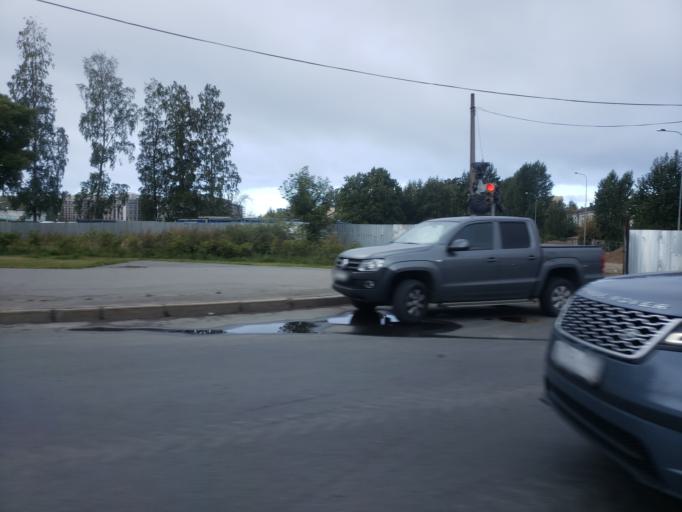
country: RU
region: St.-Petersburg
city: Vasyl'evsky Ostrov
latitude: 59.9340
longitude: 30.2350
